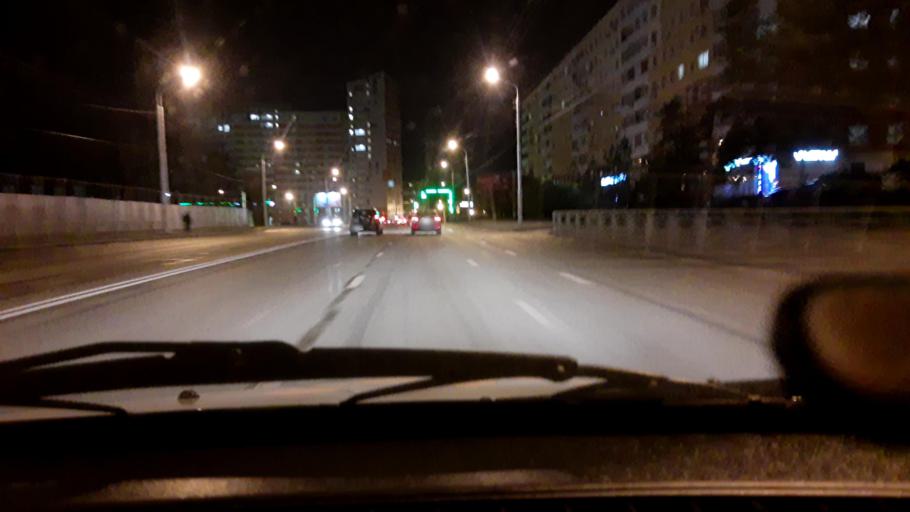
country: RU
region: Bashkortostan
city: Ufa
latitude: 54.7641
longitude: 56.0244
